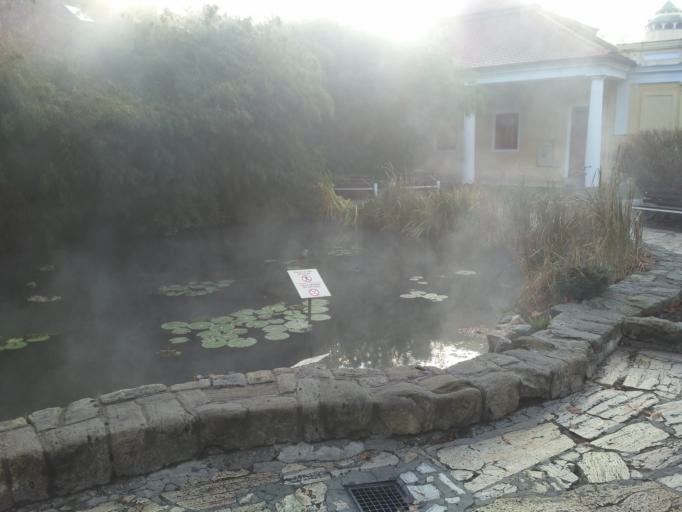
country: SK
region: Trnavsky
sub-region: Okres Trnava
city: Piestany
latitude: 48.5874
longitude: 17.8425
